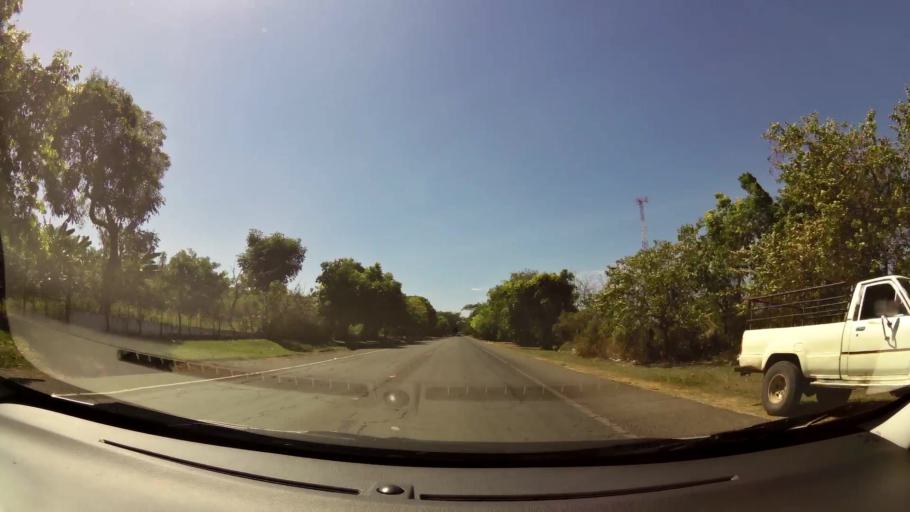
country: SV
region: Ahuachapan
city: Ahuachapan
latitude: 13.9536
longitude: -89.8337
